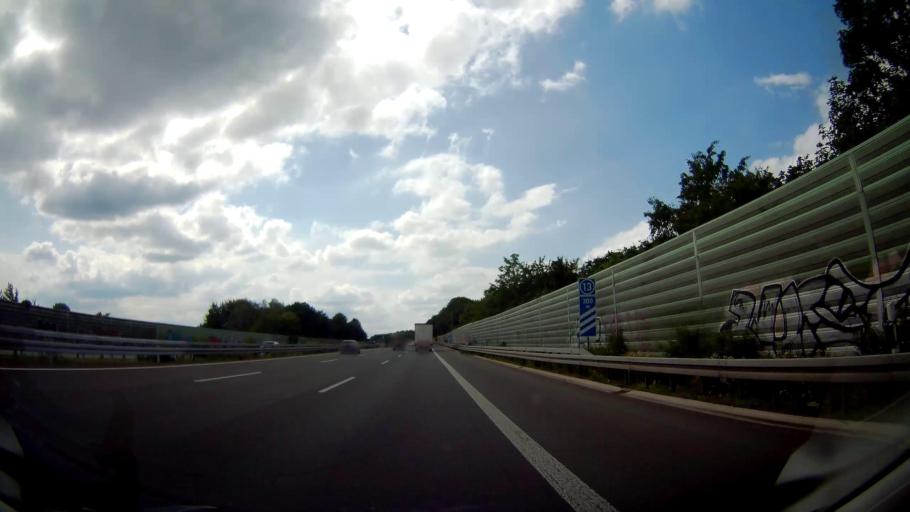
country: DE
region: North Rhine-Westphalia
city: Lunen
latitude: 51.5781
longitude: 7.5070
